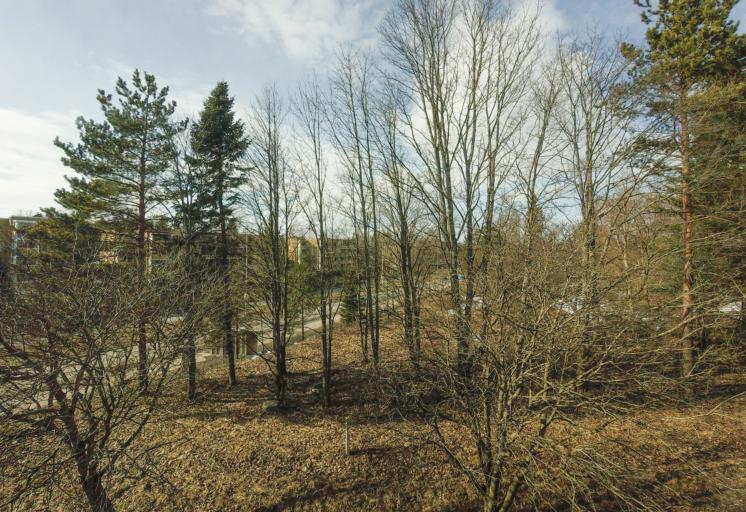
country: FI
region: South Karelia
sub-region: Imatra
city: Ruokolahti
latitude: 61.2280
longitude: 28.8609
